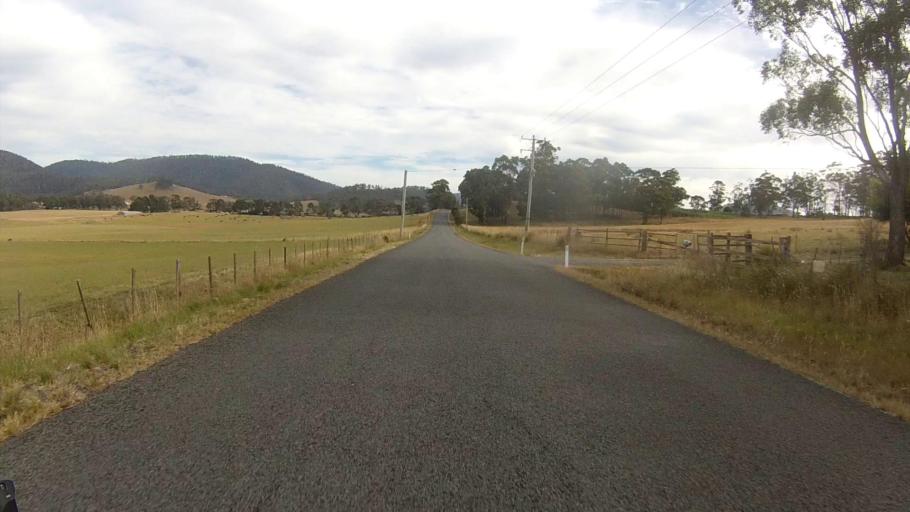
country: AU
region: Tasmania
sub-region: Sorell
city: Sorell
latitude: -42.7993
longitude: 147.7937
